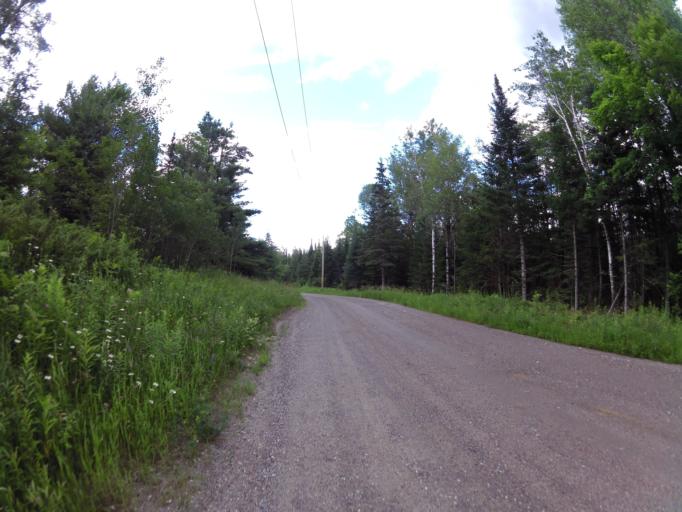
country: CA
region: Ontario
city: Renfrew
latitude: 45.0598
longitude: -76.7540
